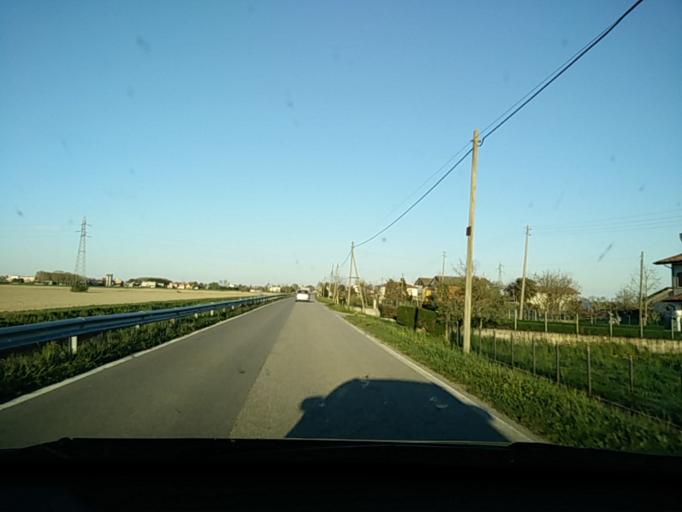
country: IT
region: Veneto
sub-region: Provincia di Venezia
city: Musile di Piave
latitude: 45.6059
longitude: 12.5435
